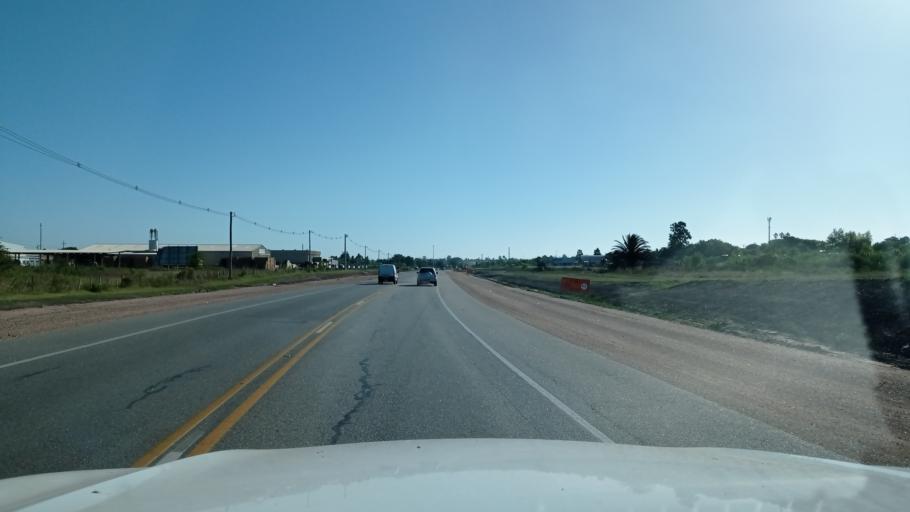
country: UY
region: Canelones
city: Pando
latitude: -34.7260
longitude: -55.9501
